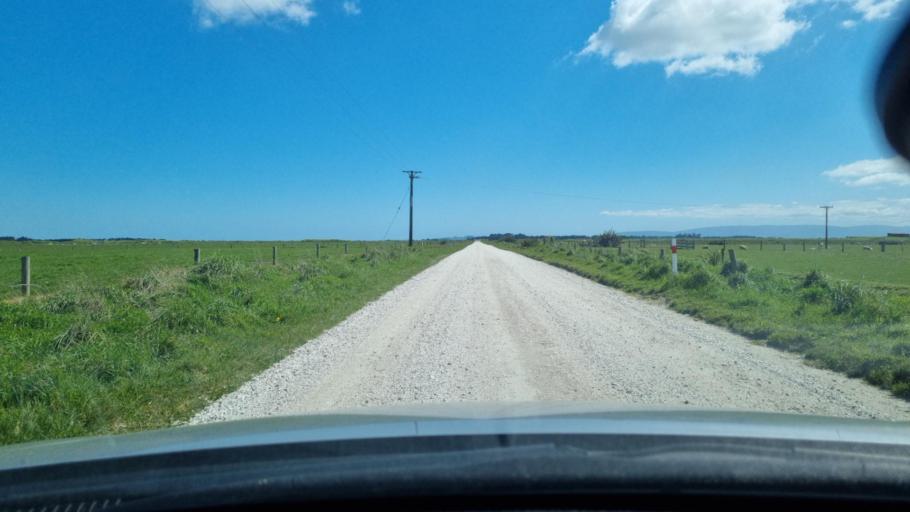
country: NZ
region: Southland
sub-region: Invercargill City
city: Invercargill
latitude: -46.3693
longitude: 168.2612
